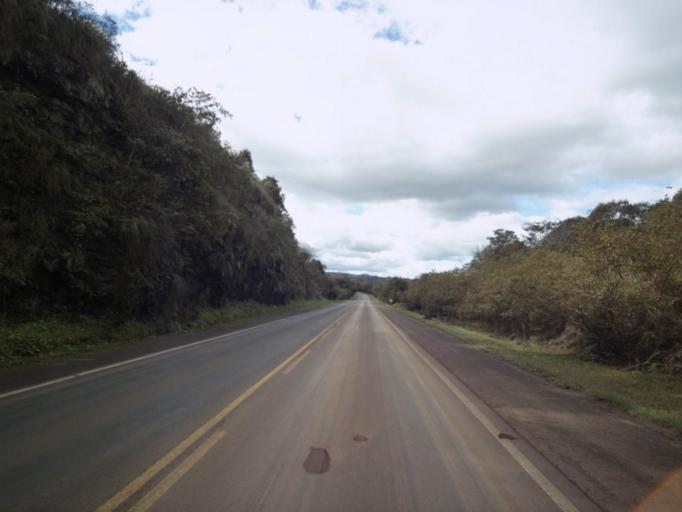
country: BR
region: Santa Catarina
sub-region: Concordia
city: Concordia
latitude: -27.3594
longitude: -51.9933
